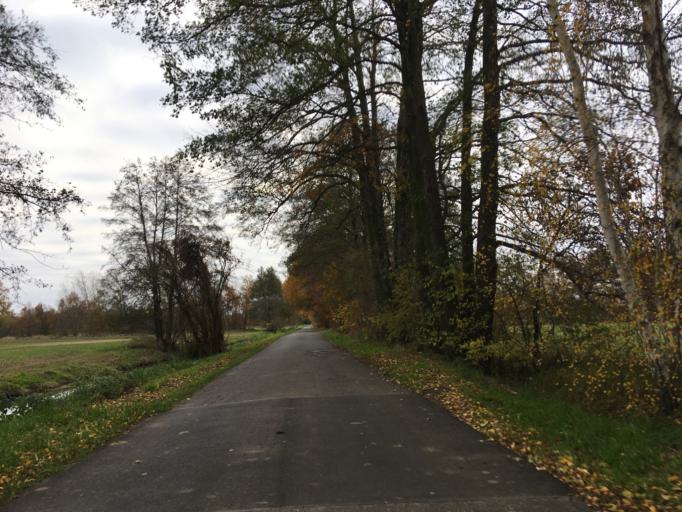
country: DE
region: Brandenburg
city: Werben
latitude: 51.8410
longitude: 14.1863
